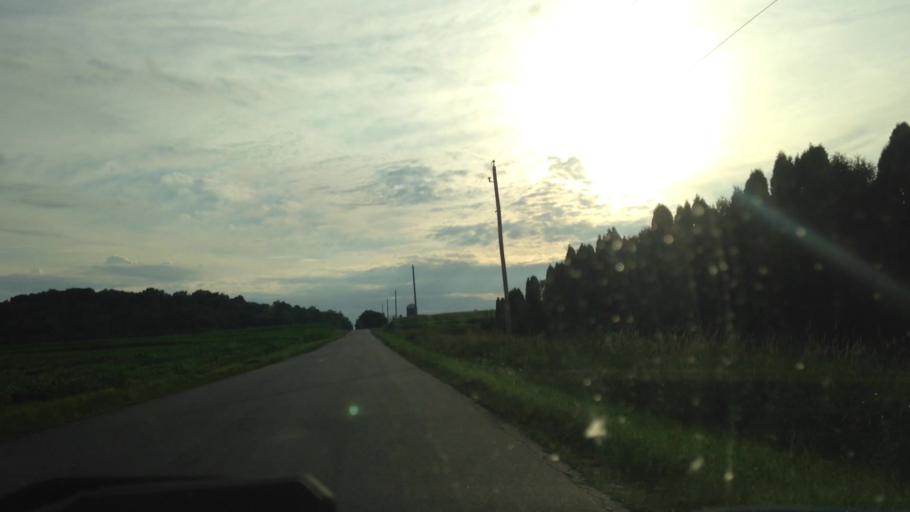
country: US
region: Wisconsin
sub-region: Dodge County
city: Theresa
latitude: 43.4860
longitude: -88.4684
